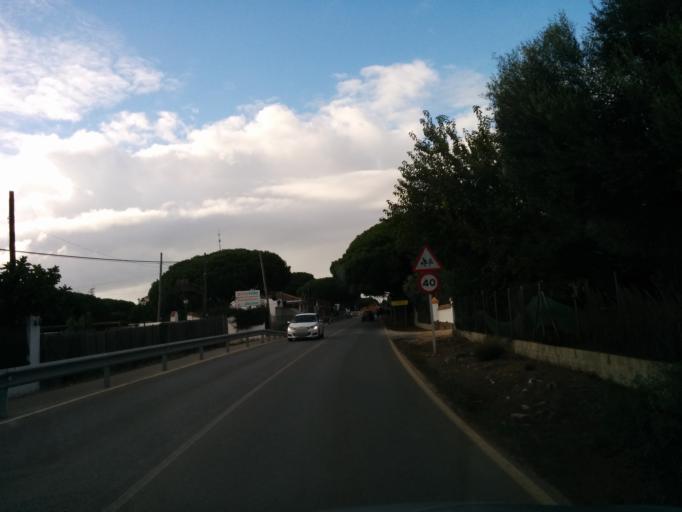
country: ES
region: Andalusia
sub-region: Provincia de Cadiz
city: Vejer de la Frontera
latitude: 36.1995
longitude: -6.0342
